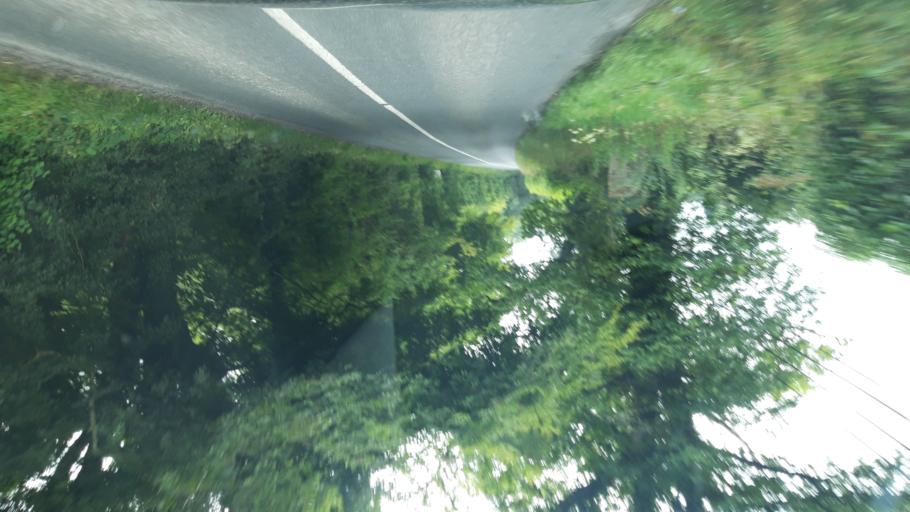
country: IE
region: Munster
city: Fethard
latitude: 52.5356
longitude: -7.6816
